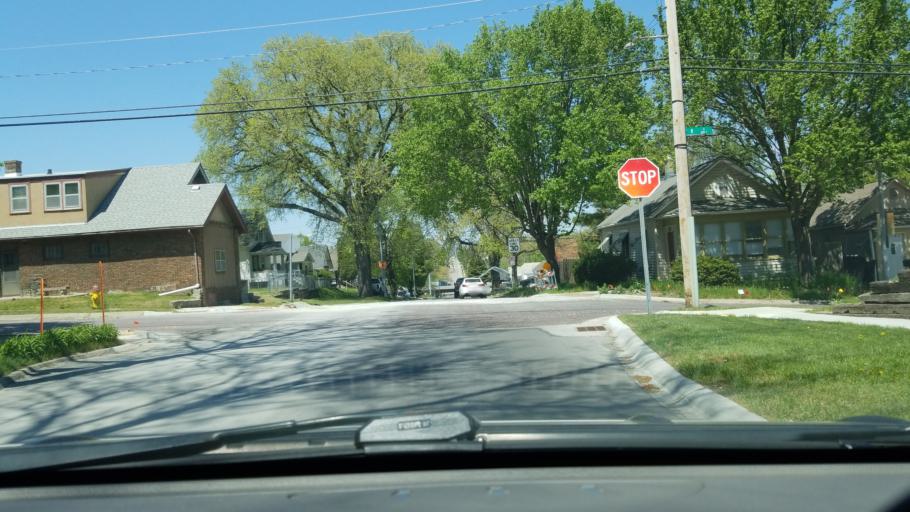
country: US
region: Nebraska
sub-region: Douglas County
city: Omaha
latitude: 41.2249
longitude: -95.9374
